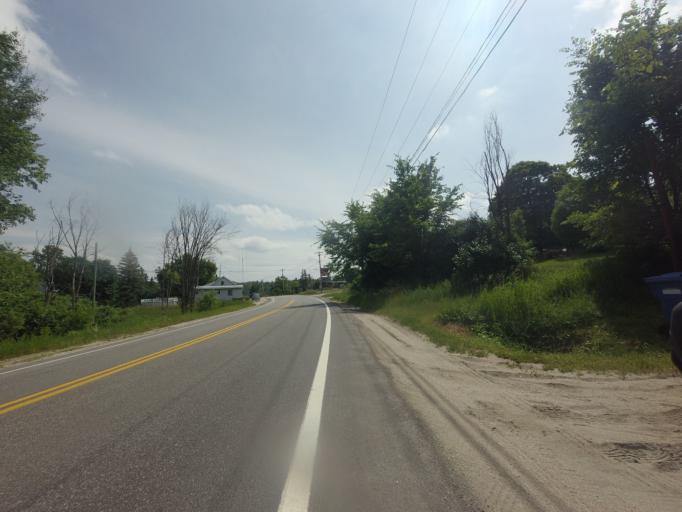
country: CA
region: Quebec
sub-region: Outaouais
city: Wakefield
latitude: 45.7846
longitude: -75.9505
